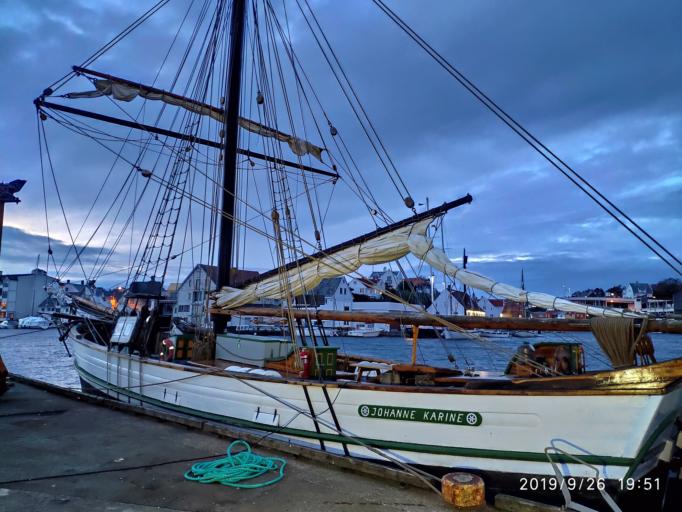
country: NO
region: Rogaland
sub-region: Haugesund
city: Haugesund
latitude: 59.4138
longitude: 5.2629
